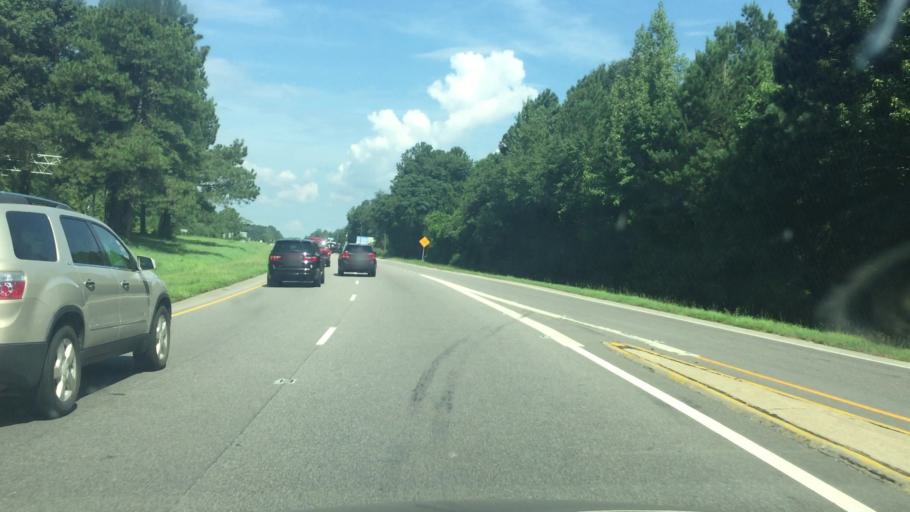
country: US
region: North Carolina
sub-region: Scotland County
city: Laurinburg
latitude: 34.7887
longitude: -79.5053
